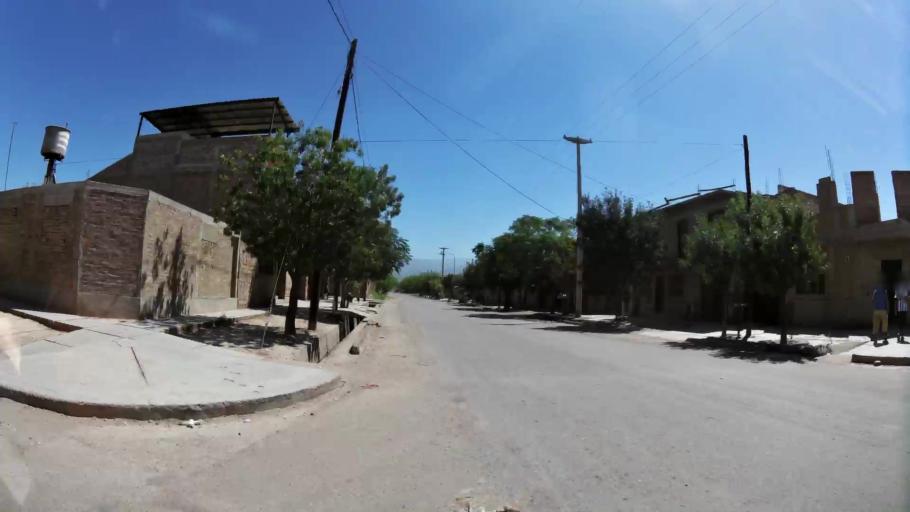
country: AR
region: Mendoza
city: Villa Nueva
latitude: -32.8787
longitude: -68.7977
